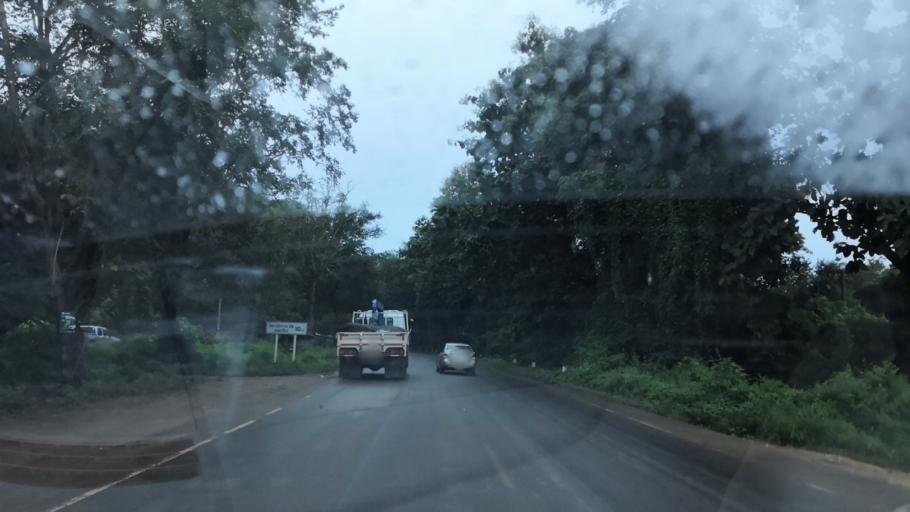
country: TH
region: Mae Hong Son
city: Pa Pae
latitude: 18.1889
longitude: 97.9358
